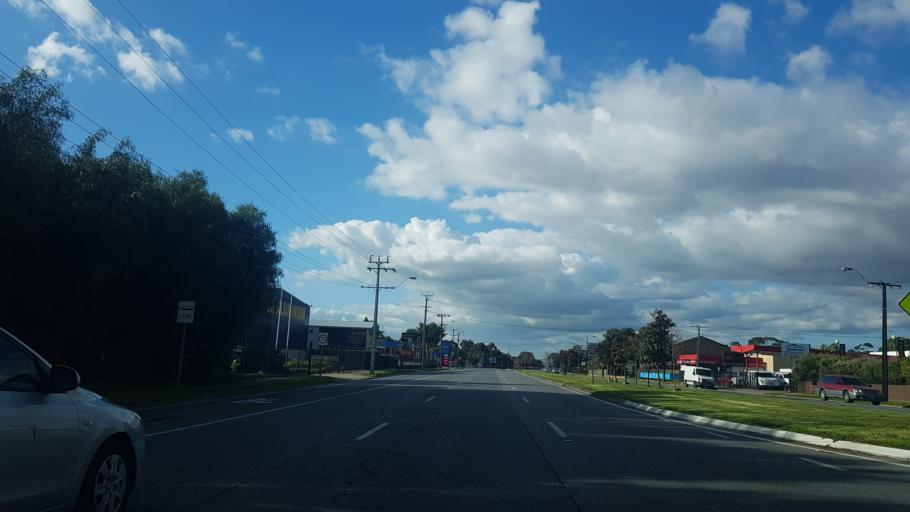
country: AU
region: South Australia
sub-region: Salisbury
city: Ingle Farm
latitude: -34.8284
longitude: 138.6143
